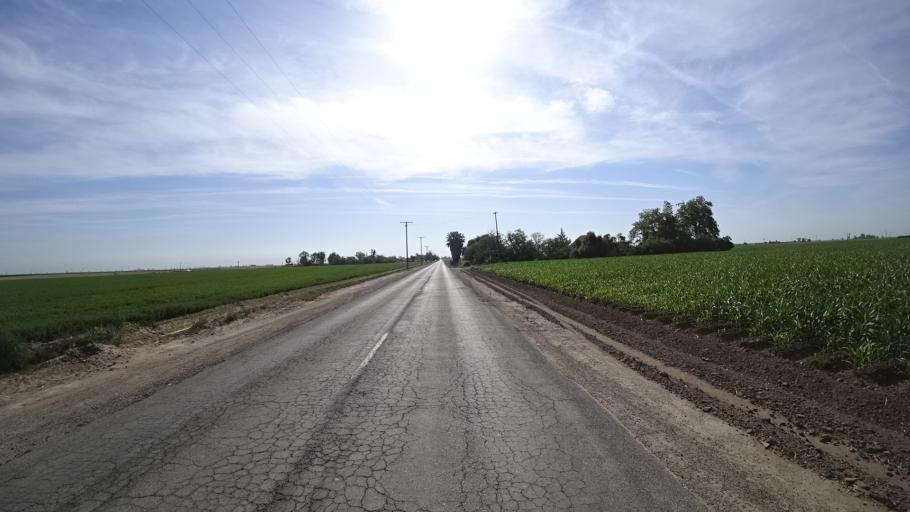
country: US
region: California
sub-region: Tulare County
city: Goshen
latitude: 36.3492
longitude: -119.4805
